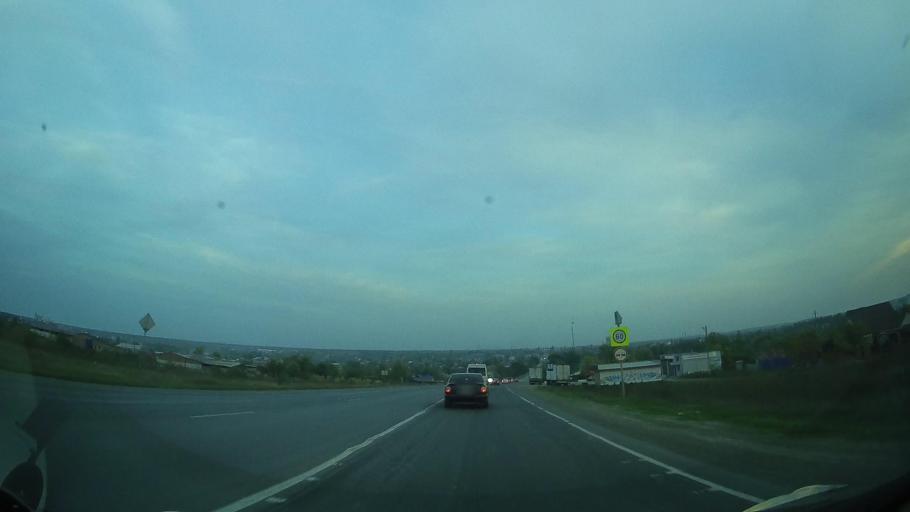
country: RU
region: Rostov
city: Kagal'nitskaya
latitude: 46.8878
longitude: 40.1403
